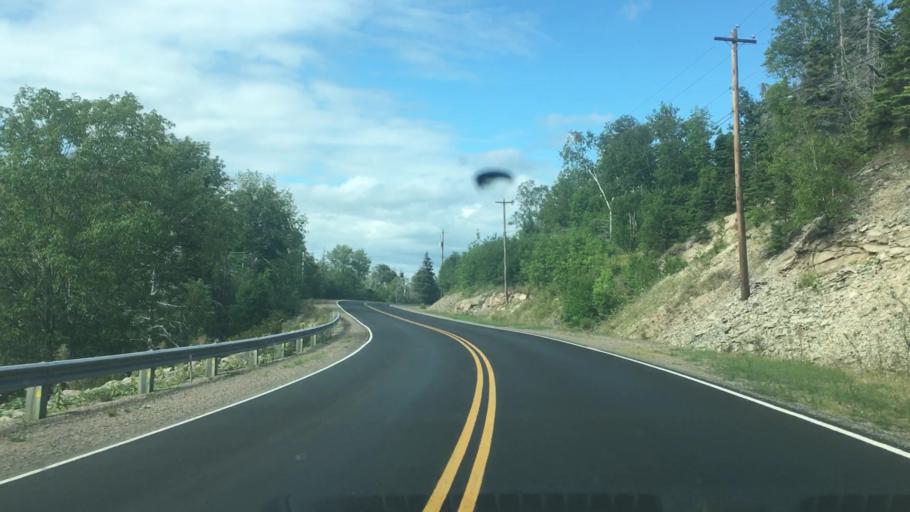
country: CA
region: Nova Scotia
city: Princeville
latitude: 45.7931
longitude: -60.7370
